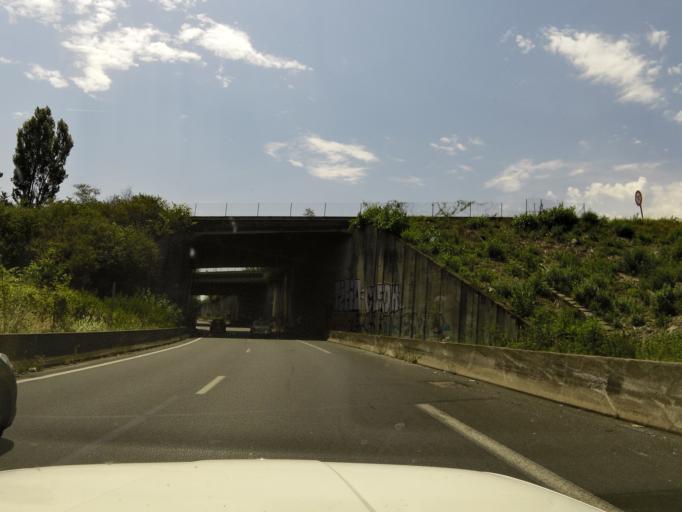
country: FR
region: Rhone-Alpes
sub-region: Departement du Rhone
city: Vaulx-en-Velin
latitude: 45.8063
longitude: 4.9251
